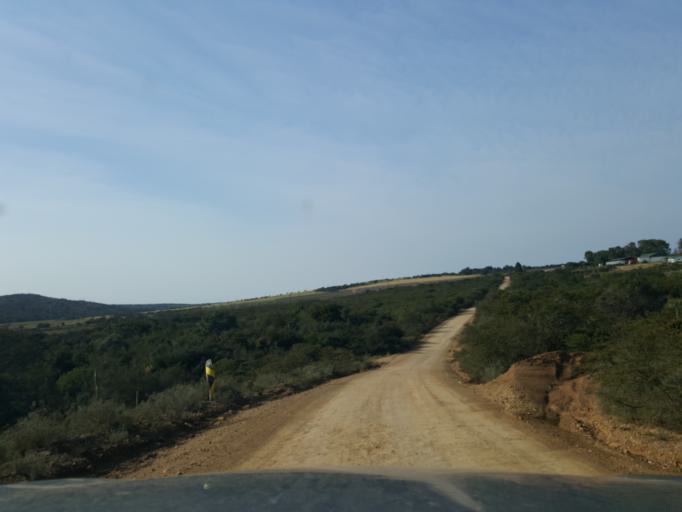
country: ZA
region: Eastern Cape
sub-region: Cacadu District Municipality
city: Grahamstown
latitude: -33.4104
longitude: 26.3062
